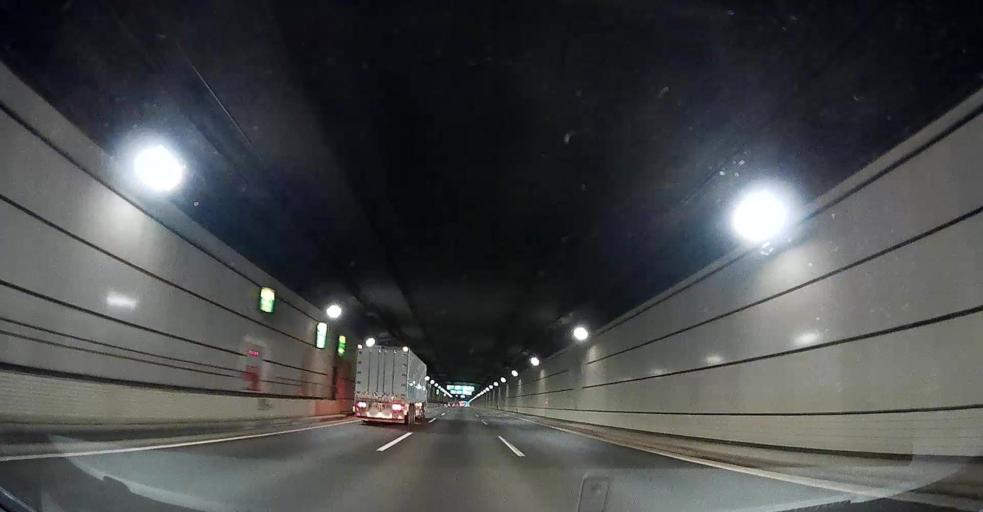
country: JP
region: Kanagawa
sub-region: Kawasaki-shi
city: Kawasaki
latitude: 35.5279
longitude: 139.7935
